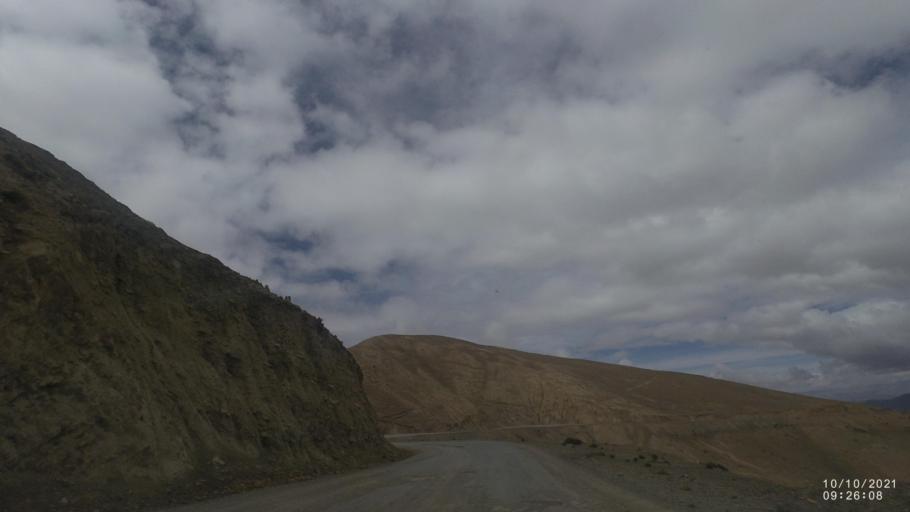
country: BO
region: La Paz
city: Quime
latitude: -17.0944
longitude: -67.3194
